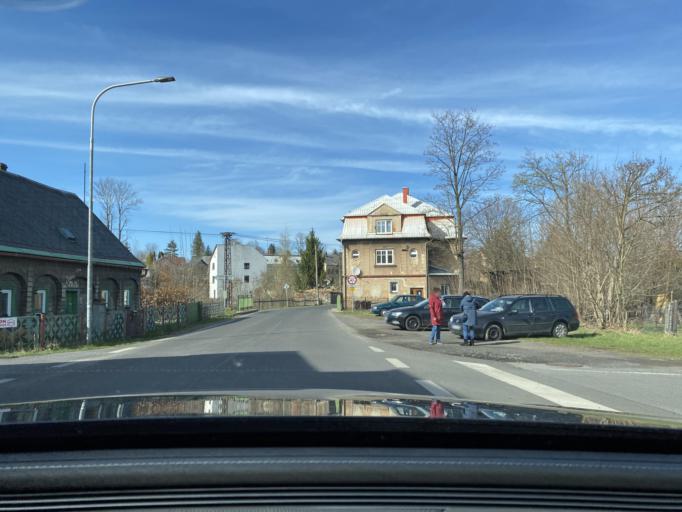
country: CZ
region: Ustecky
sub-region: Okres Decin
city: Sluknov
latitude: 51.0053
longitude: 14.4526
